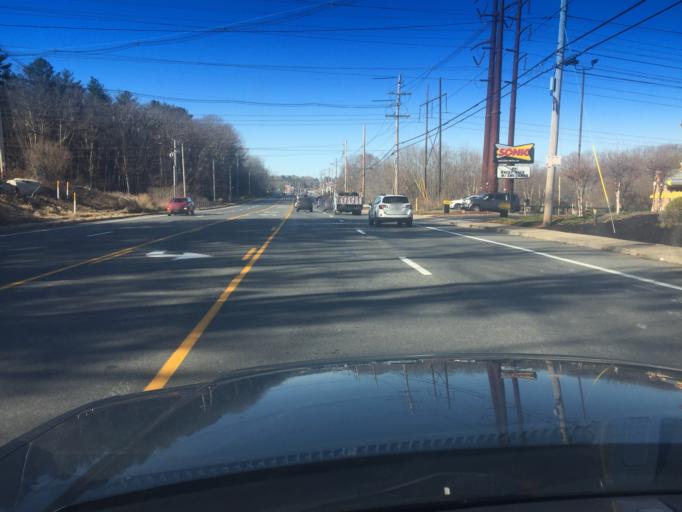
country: US
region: Rhode Island
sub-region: Providence County
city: Greenville
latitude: 41.8702
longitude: -71.5238
